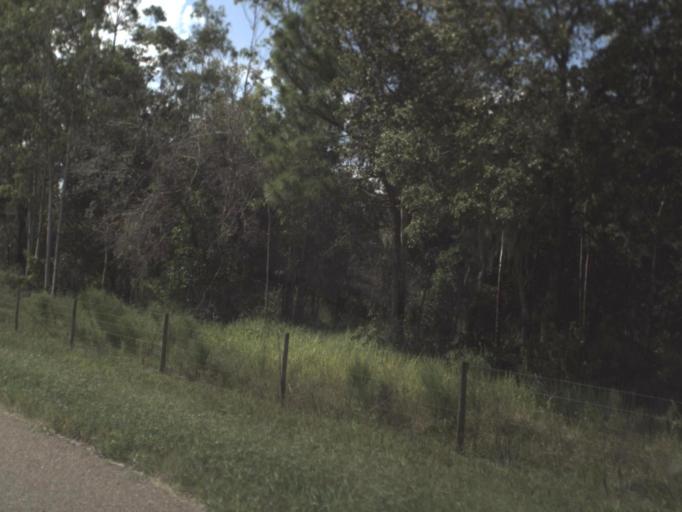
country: US
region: Florida
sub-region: Hardee County
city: Wauchula
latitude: 27.4880
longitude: -82.0197
